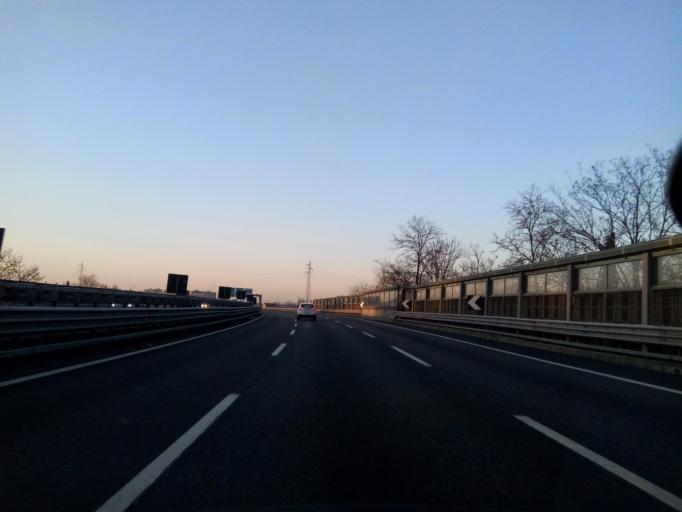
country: IT
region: Lombardy
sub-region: Citta metropolitana di Milano
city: Settimo Milanese
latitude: 45.4644
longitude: 9.0761
